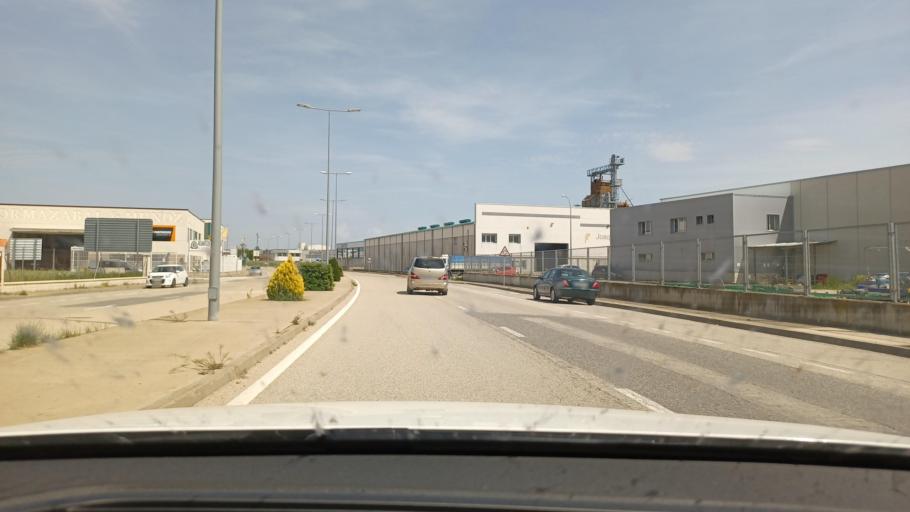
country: ES
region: Castille and Leon
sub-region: Provincia de Soria
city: Almazan
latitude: 41.4703
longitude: -2.5380
